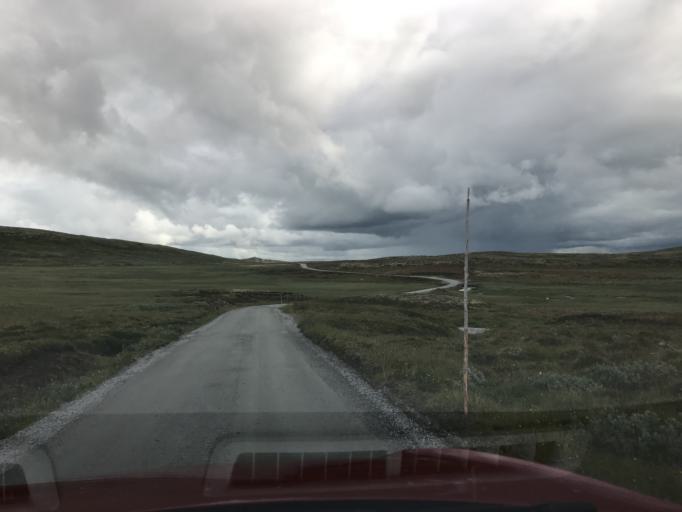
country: NO
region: Buskerud
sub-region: Hol
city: Geilo
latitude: 60.5510
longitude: 8.0746
